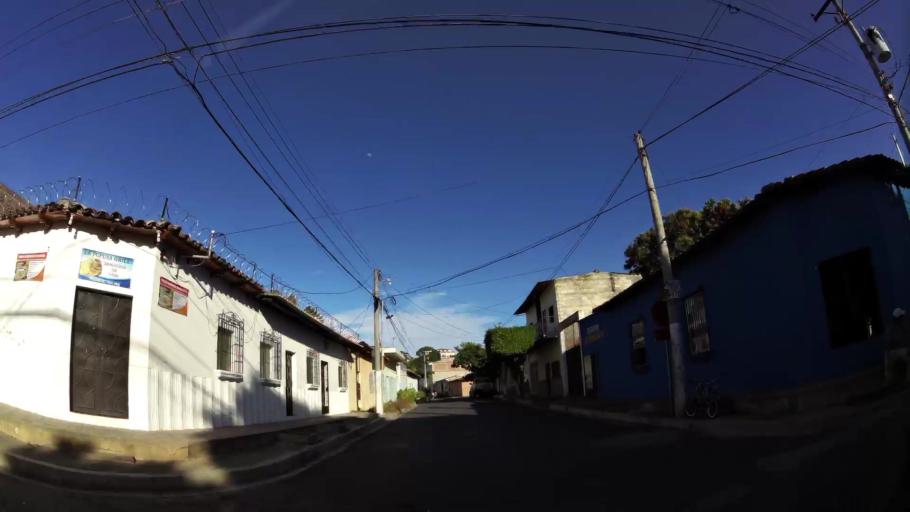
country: SV
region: Santa Ana
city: Metapan
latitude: 14.3339
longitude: -89.4480
